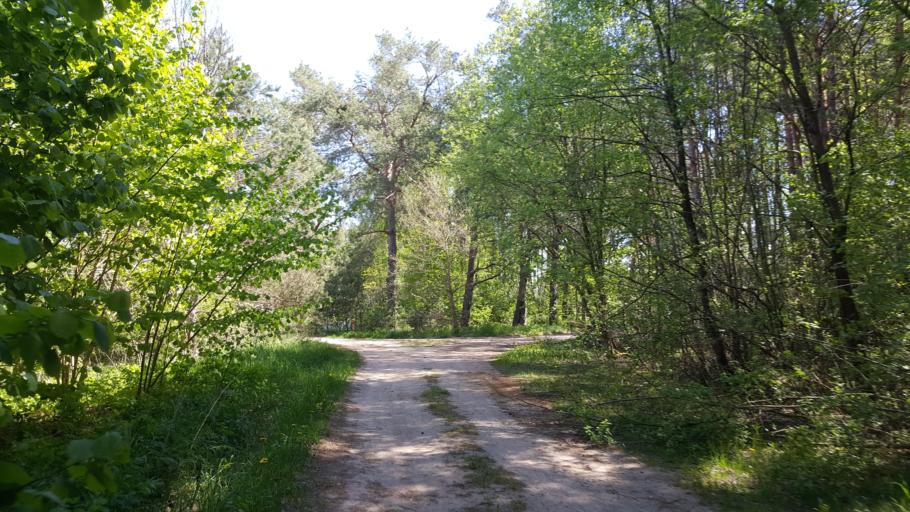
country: BY
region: Brest
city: Zhabinka
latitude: 52.3780
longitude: 24.0206
